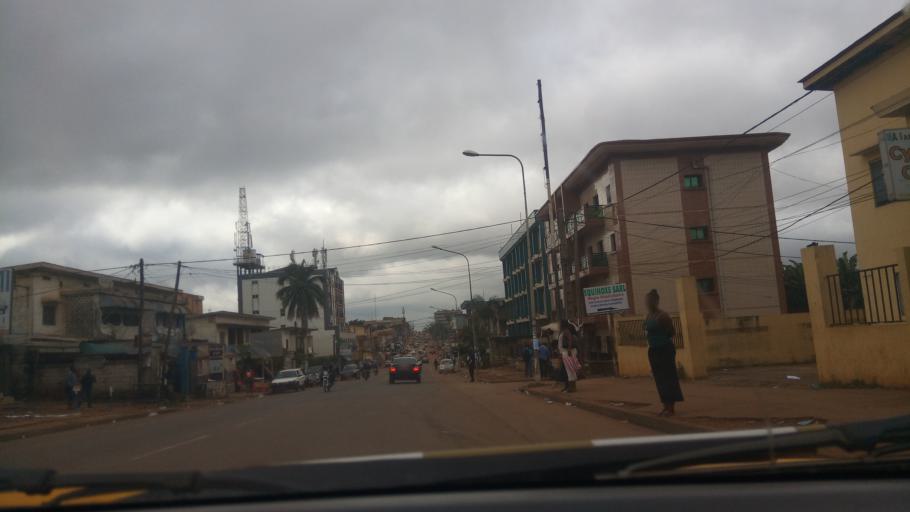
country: CM
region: Centre
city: Yaounde
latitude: 3.8862
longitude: 11.5017
